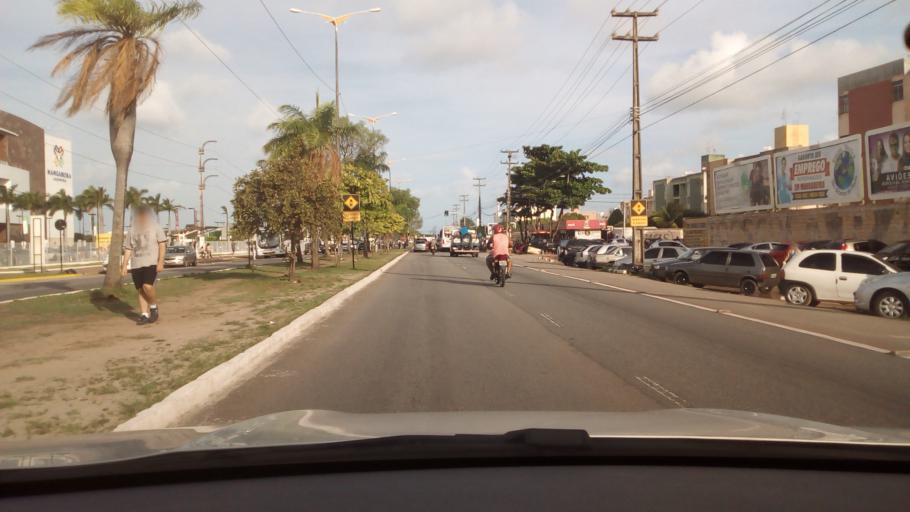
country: BR
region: Paraiba
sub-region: Joao Pessoa
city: Joao Pessoa
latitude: -7.1632
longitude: -34.8320
